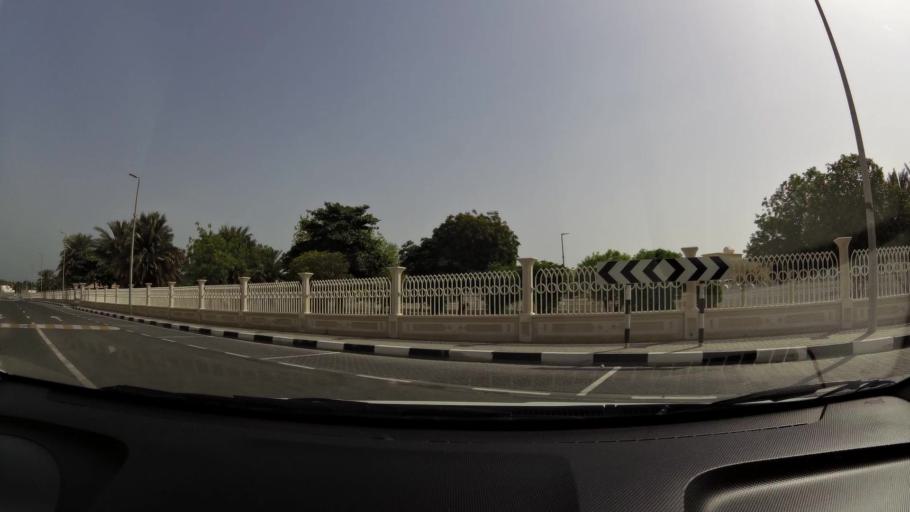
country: AE
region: Ash Shariqah
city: Sharjah
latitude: 25.3499
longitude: 55.4190
